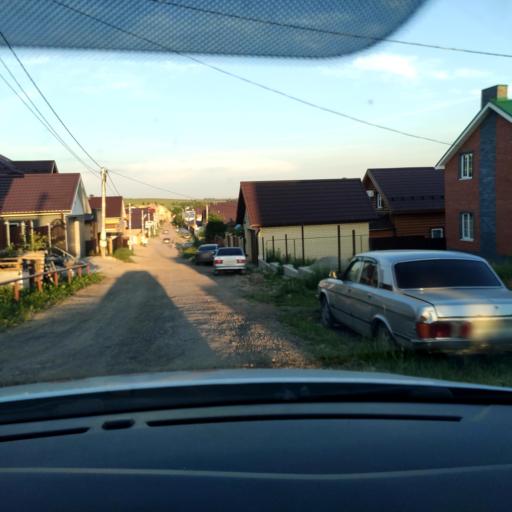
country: RU
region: Tatarstan
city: Stolbishchi
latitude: 55.7518
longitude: 49.3033
